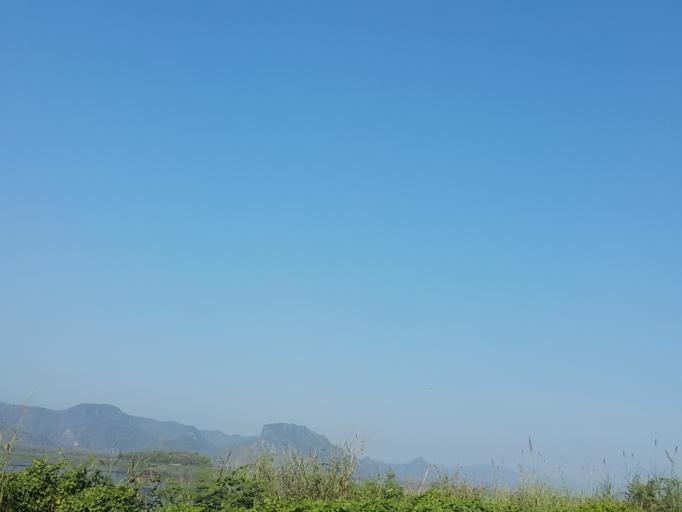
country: TH
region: Sukhothai
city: Thung Saliam
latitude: 17.3060
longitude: 99.4241
